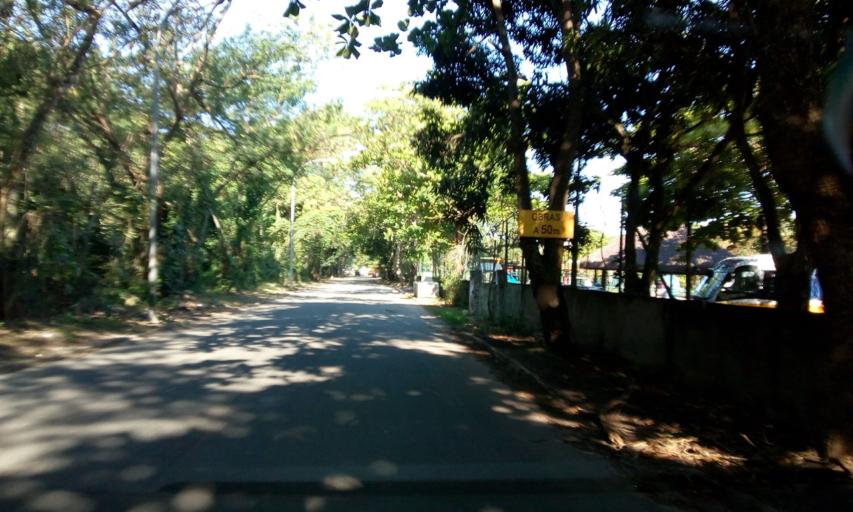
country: BR
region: Rio de Janeiro
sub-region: Nilopolis
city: Nilopolis
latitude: -22.9950
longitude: -43.3860
